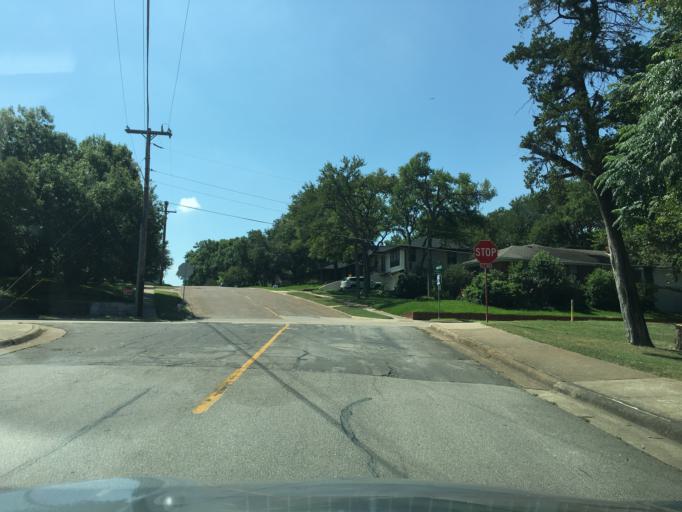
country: US
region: Texas
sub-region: Dallas County
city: Garland
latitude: 32.8550
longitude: -96.6926
